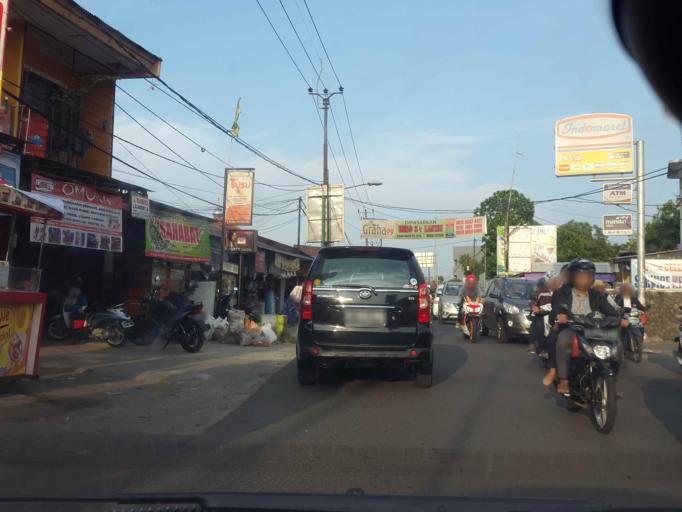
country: ID
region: Banten
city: South Tangerang
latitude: -6.2627
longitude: 106.7368
